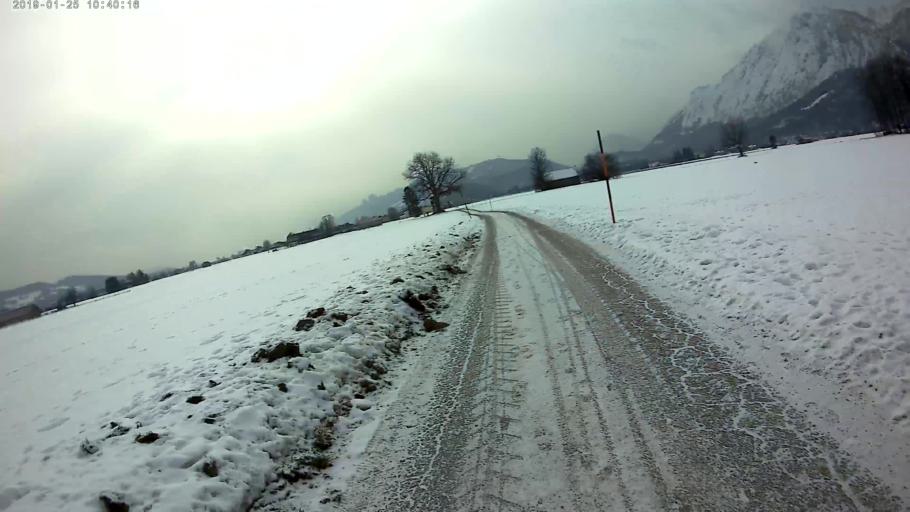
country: AT
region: Salzburg
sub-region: Politischer Bezirk Salzburg-Umgebung
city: Anif
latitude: 47.7529
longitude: 13.0480
